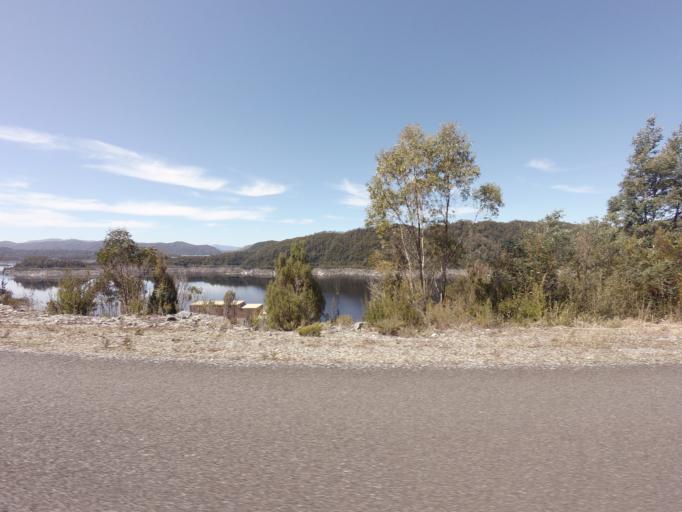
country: AU
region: Tasmania
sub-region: West Coast
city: Queenstown
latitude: -42.7409
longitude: 145.9809
